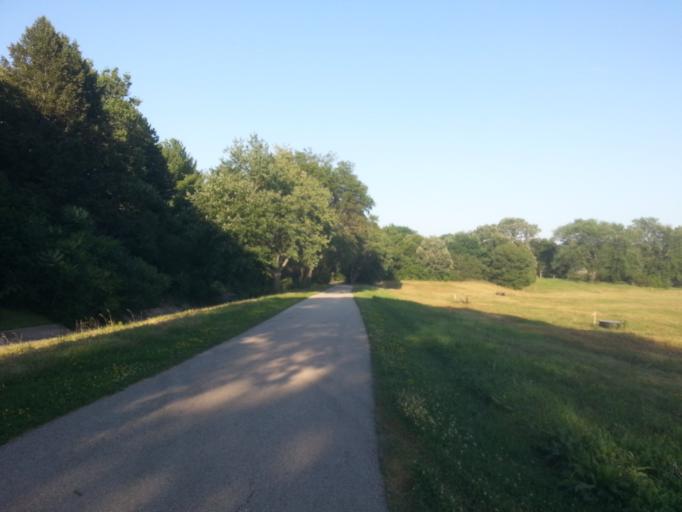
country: US
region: Wisconsin
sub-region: Dane County
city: Middleton
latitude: 43.0655
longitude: -89.4961
